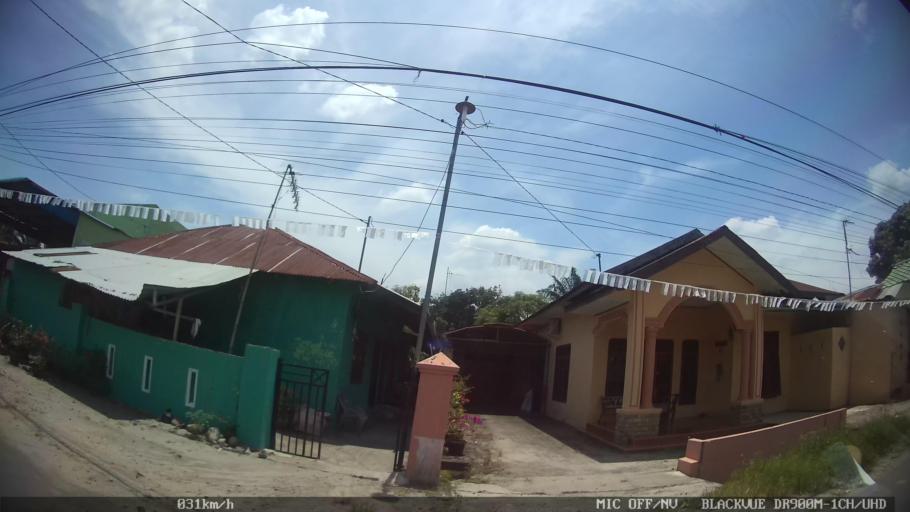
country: ID
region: North Sumatra
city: Binjai
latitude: 3.6033
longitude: 98.5181
